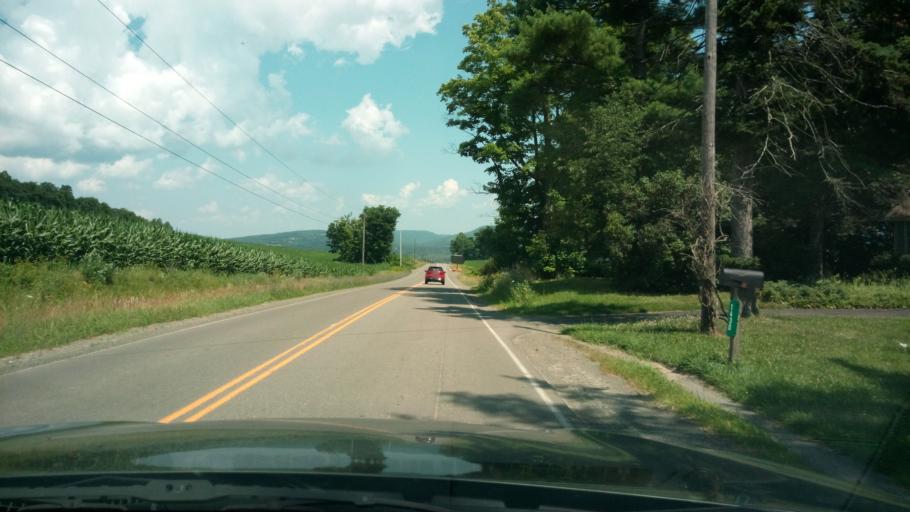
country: US
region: New York
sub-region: Schuyler County
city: Montour Falls
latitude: 42.3026
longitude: -76.7849
